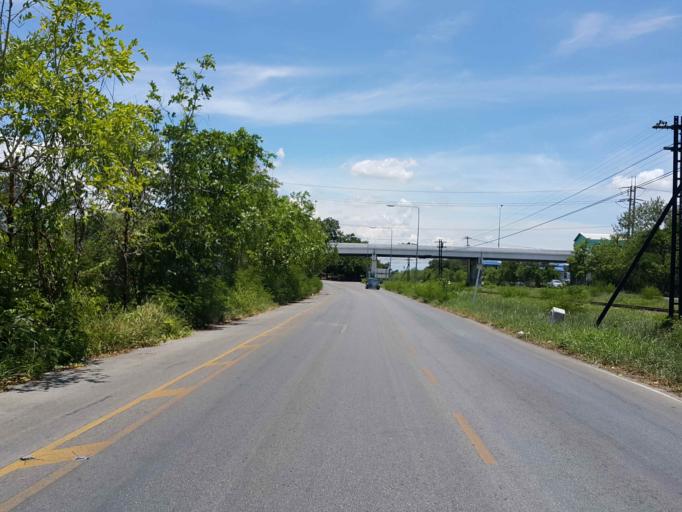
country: TH
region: Chiang Mai
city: Chiang Mai
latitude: 18.7597
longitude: 99.0203
